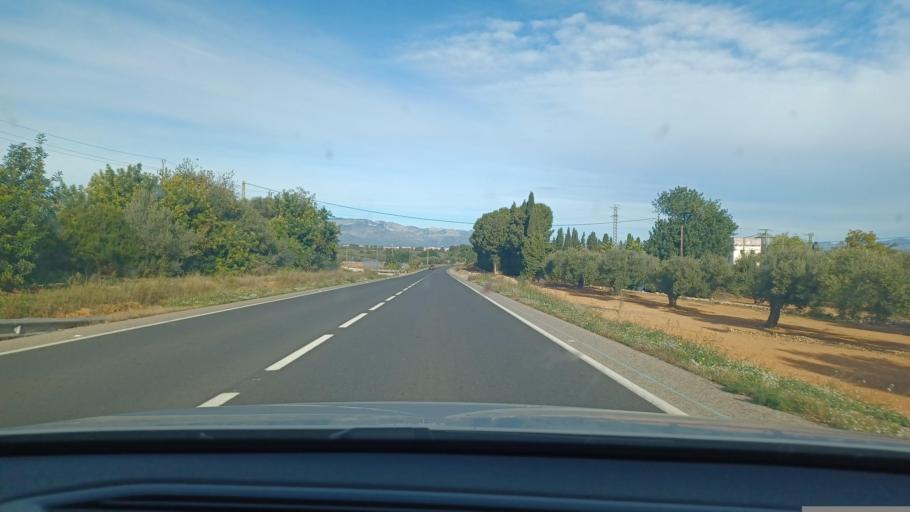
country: ES
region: Catalonia
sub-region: Provincia de Tarragona
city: Santa Barbara
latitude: 40.6853
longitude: 0.5092
